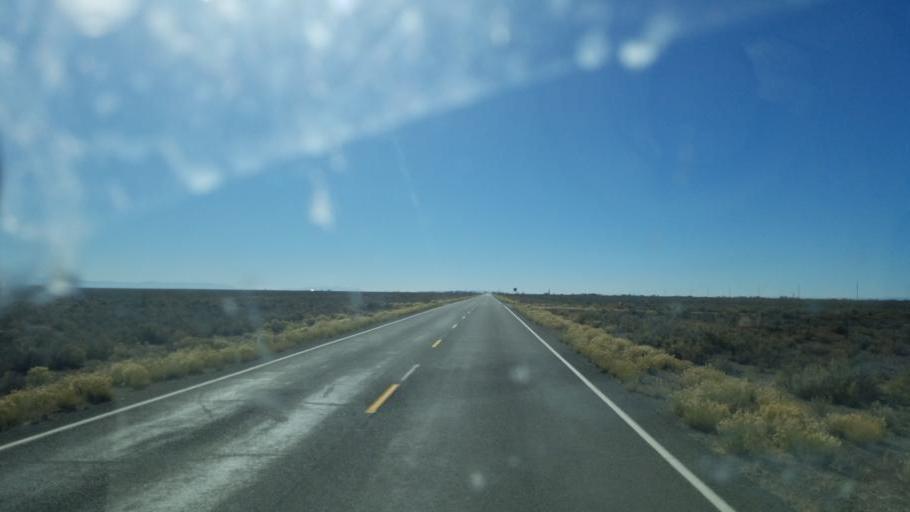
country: US
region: Colorado
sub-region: Saguache County
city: Center
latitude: 37.8087
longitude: -105.8874
